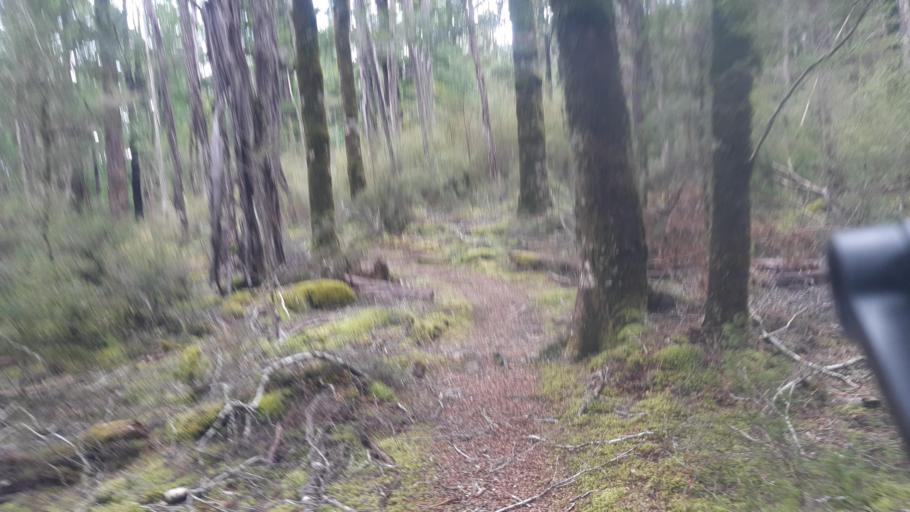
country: NZ
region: Tasman
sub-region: Tasman District
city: Wakefield
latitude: -41.7749
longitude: 172.8078
